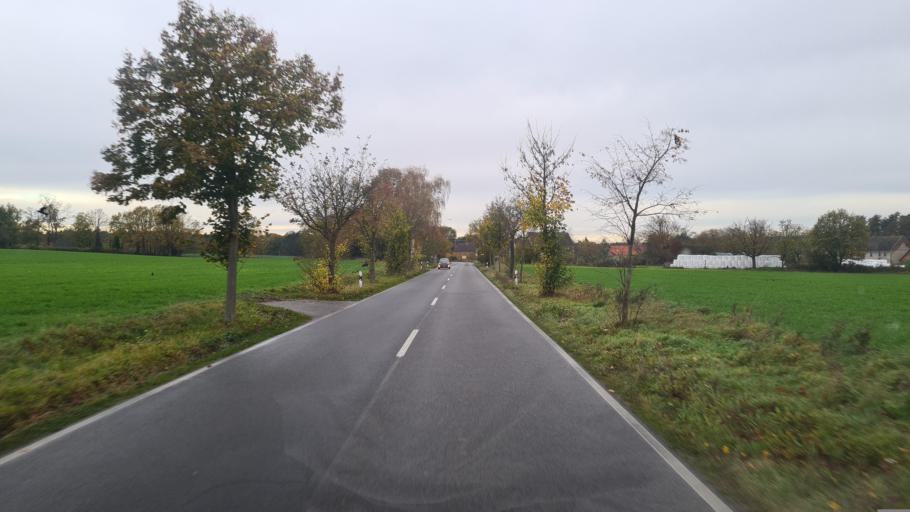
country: DE
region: Saxony-Anhalt
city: Abtsdorf
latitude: 51.9153
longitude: 12.6817
